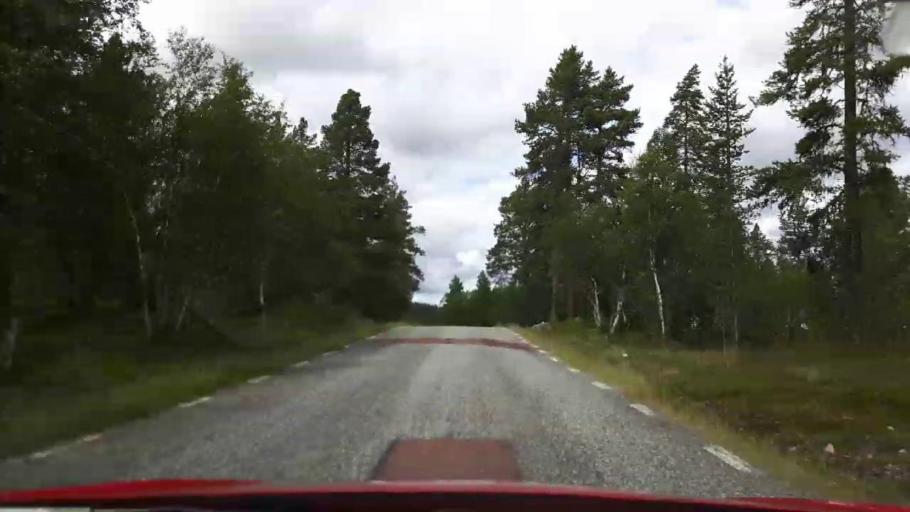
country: NO
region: Hedmark
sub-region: Trysil
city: Innbygda
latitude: 62.1179
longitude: 12.9735
